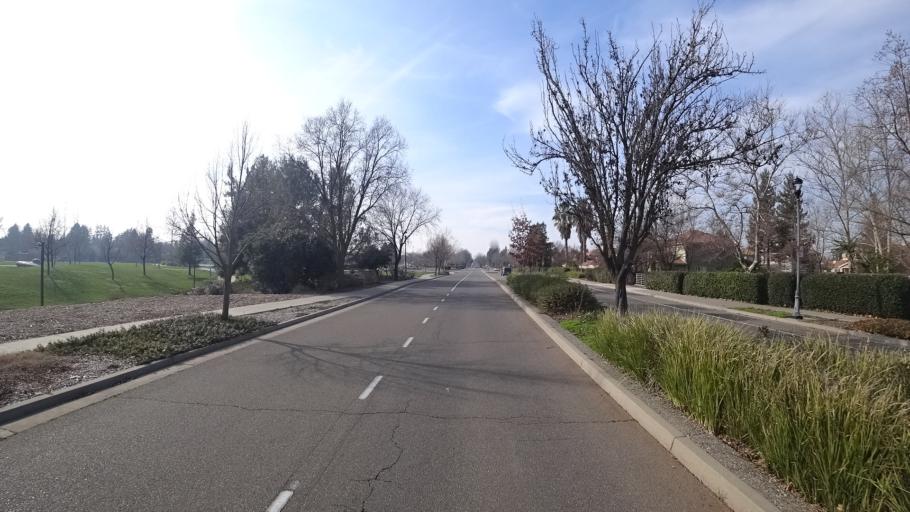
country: US
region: California
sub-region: Yolo County
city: Davis
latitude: 38.5554
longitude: -121.7732
